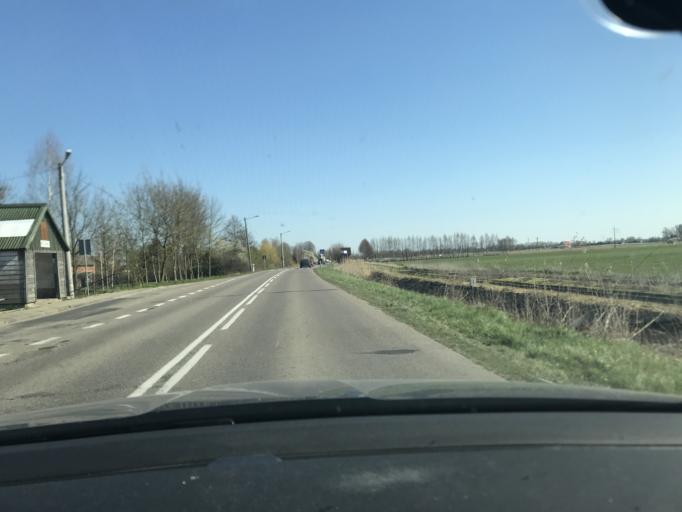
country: PL
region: Pomeranian Voivodeship
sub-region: Powiat nowodworski
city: Stegna
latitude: 54.2755
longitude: 19.1344
